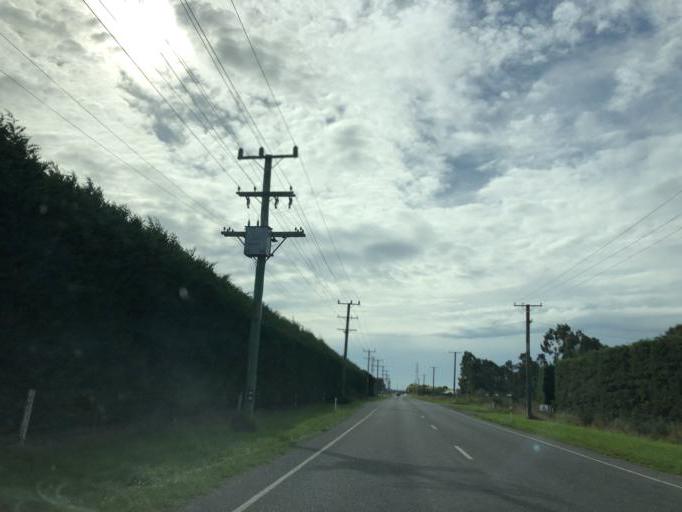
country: NZ
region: Canterbury
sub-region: Selwyn District
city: Lincoln
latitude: -43.6408
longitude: 172.4542
